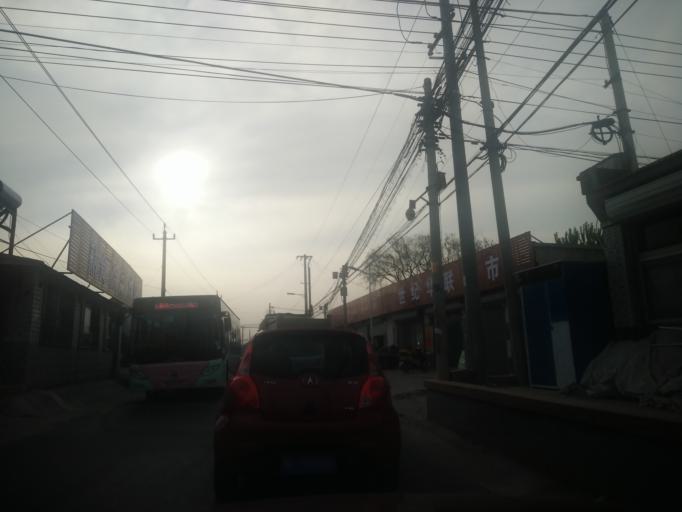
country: CN
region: Beijing
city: Qingyundian
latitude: 39.6790
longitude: 116.4788
